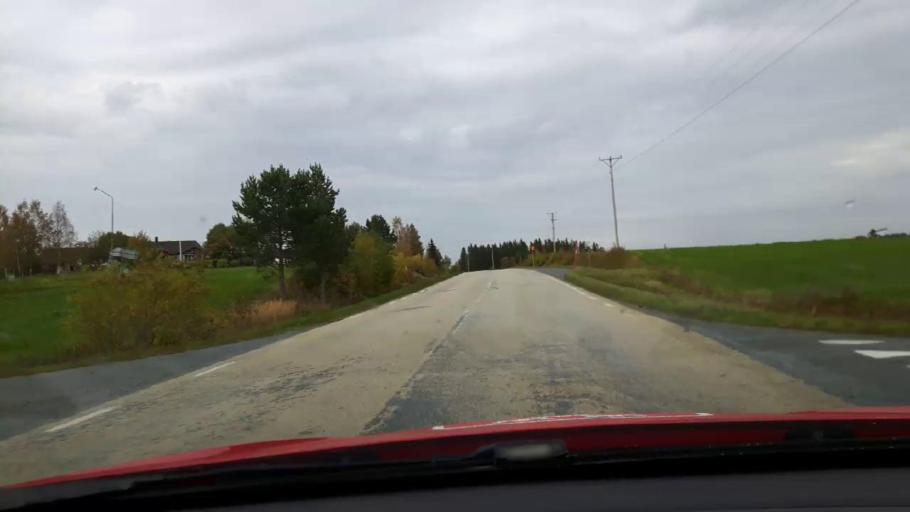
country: SE
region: Jaemtland
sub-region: Bergs Kommun
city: Hoverberg
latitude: 62.9590
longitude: 14.3452
